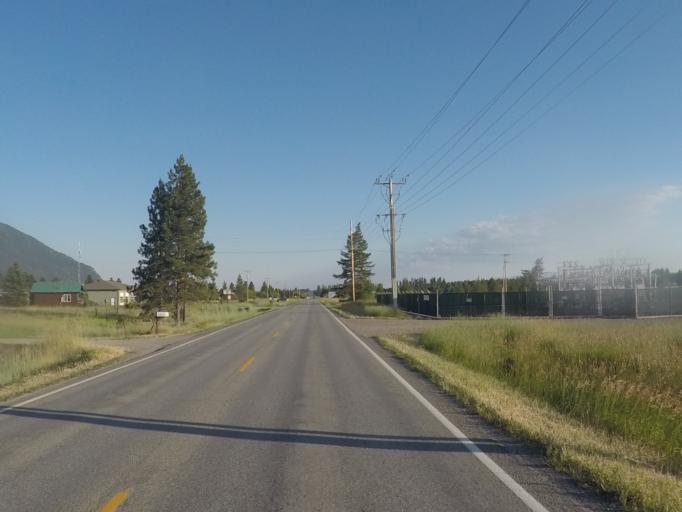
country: US
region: Montana
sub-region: Flathead County
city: Columbia Falls
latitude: 48.3512
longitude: -114.1593
